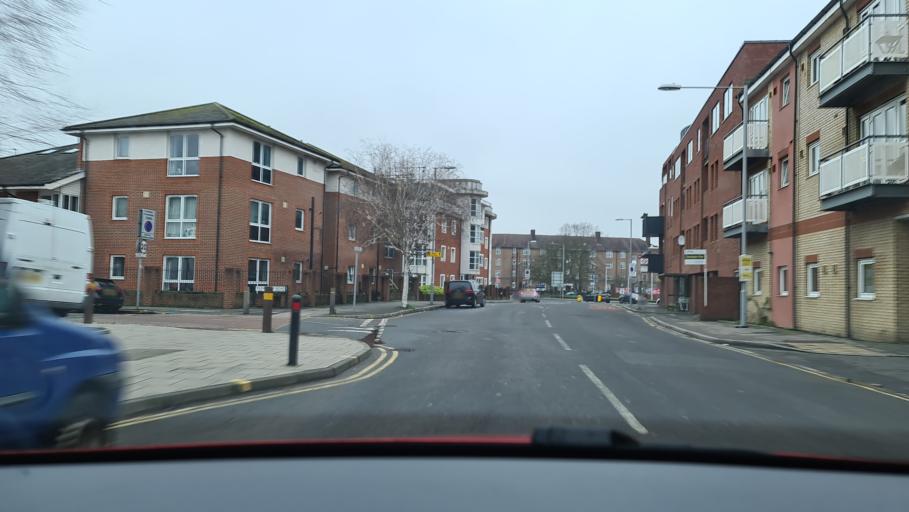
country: GB
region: England
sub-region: Greater London
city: Kingston upon Thames
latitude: 51.4123
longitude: -0.2884
